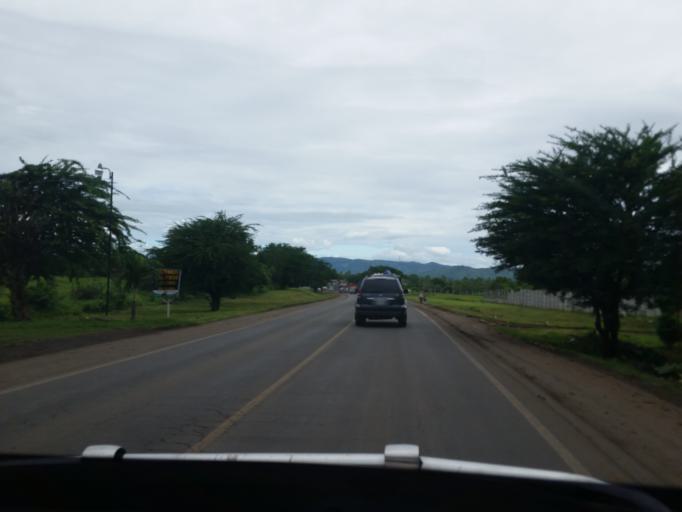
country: NI
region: Managua
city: Tipitapa
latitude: 12.2888
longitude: -86.0579
